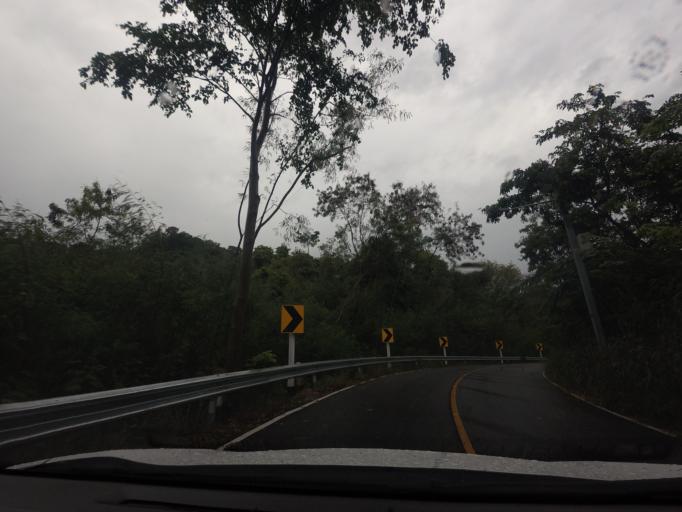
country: TH
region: Rayong
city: Ban Chang
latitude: 12.7672
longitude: 100.9521
